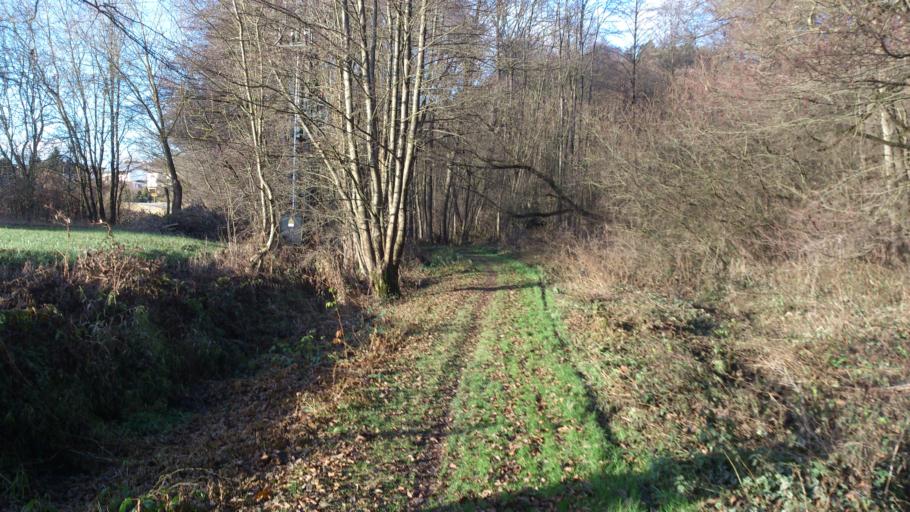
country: DE
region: Bavaria
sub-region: Upper Franconia
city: Stadtsteinach
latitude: 50.1730
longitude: 11.5028
